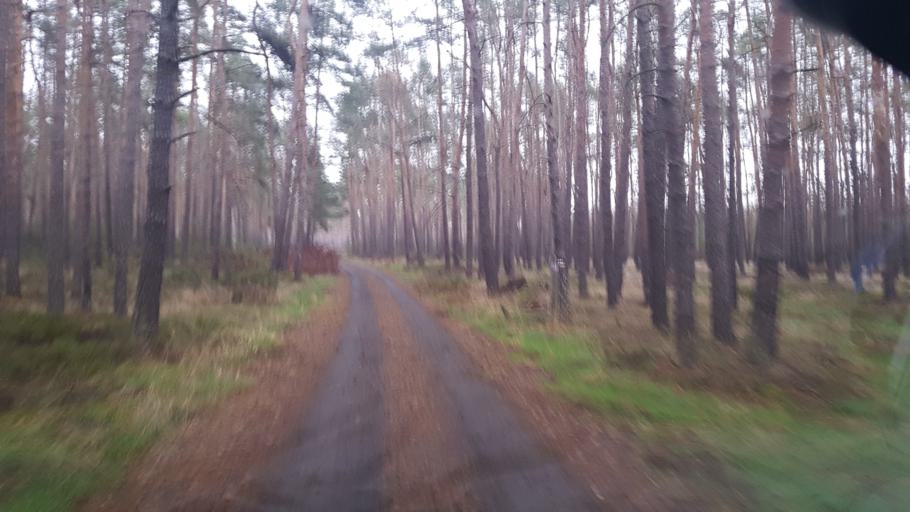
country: DE
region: Brandenburg
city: Muhlberg
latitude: 51.4964
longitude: 13.2971
